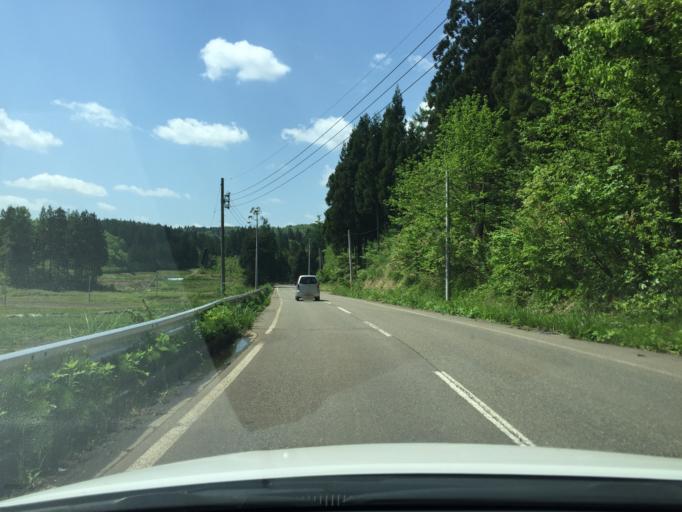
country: JP
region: Niigata
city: Tochio-honcho
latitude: 37.4715
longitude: 139.0363
